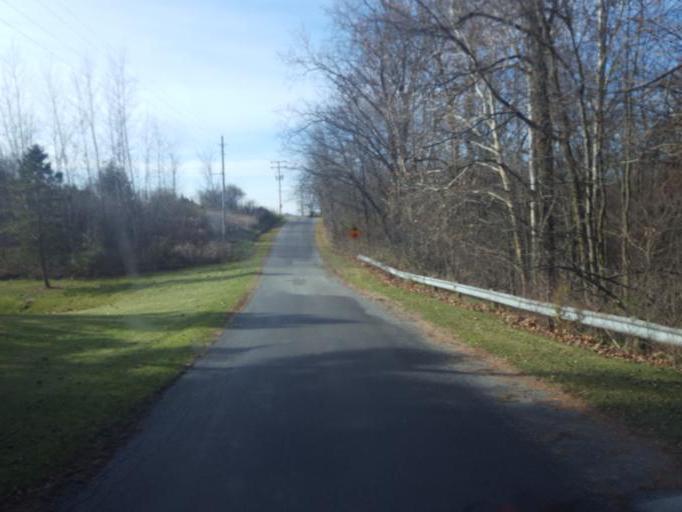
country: US
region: Ohio
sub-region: Crawford County
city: Crestline
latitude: 40.8415
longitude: -82.8162
